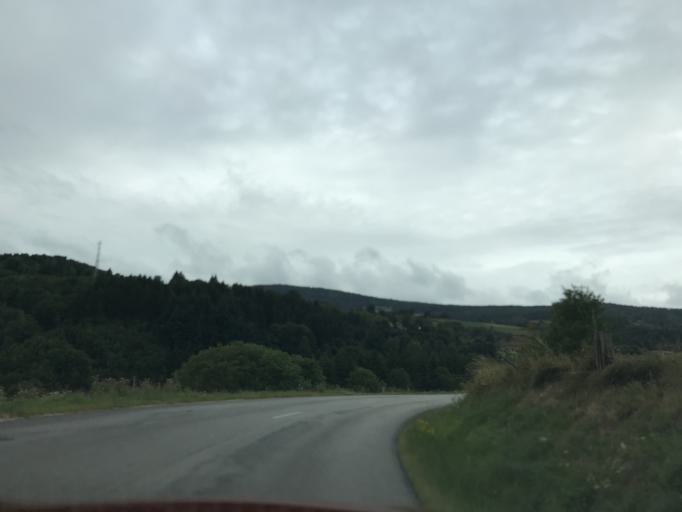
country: FR
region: Rhone-Alpes
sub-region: Departement de la Loire
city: Sail-sous-Couzan
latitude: 45.6988
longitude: 3.8573
